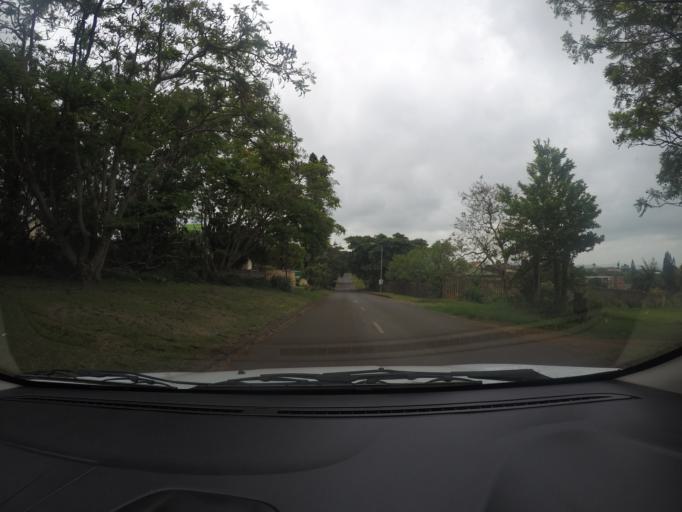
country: ZA
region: KwaZulu-Natal
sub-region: uThungulu District Municipality
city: Empangeni
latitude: -28.7454
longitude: 31.8943
